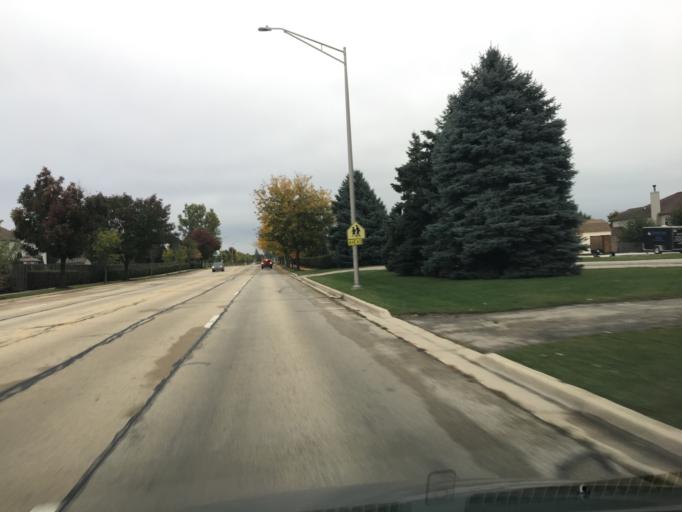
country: US
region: Illinois
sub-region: Will County
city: Plainfield
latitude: 41.6523
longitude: -88.1674
